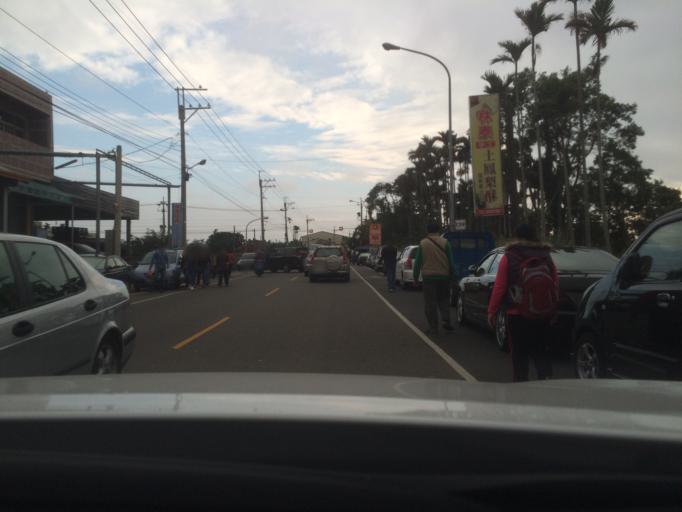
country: TW
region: Taiwan
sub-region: Nantou
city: Nantou
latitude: 23.9366
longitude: 120.6380
